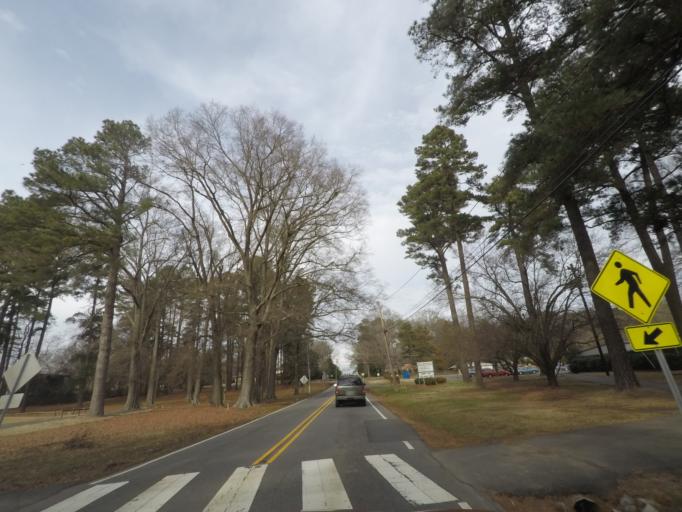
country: US
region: North Carolina
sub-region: Durham County
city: Durham
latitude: 36.0236
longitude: -78.9360
